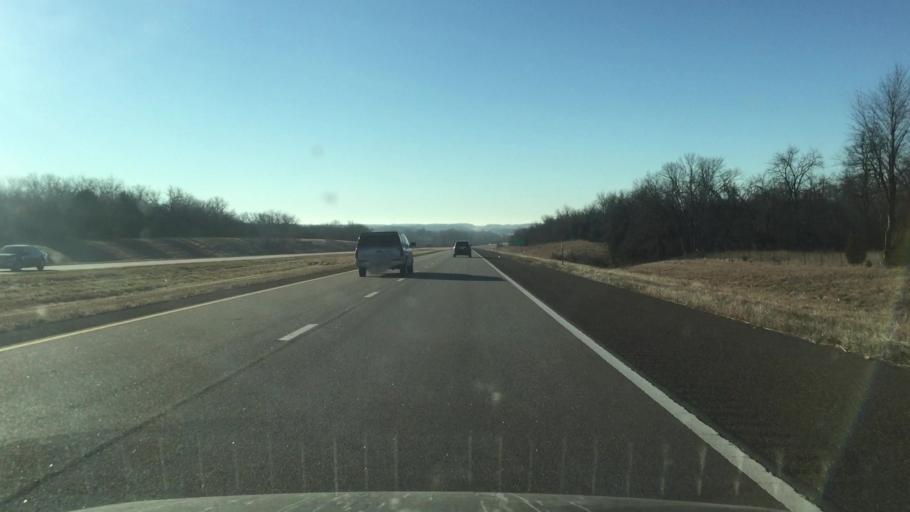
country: US
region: Kansas
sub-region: Johnson County
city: Spring Hill
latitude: 38.7147
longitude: -94.8347
